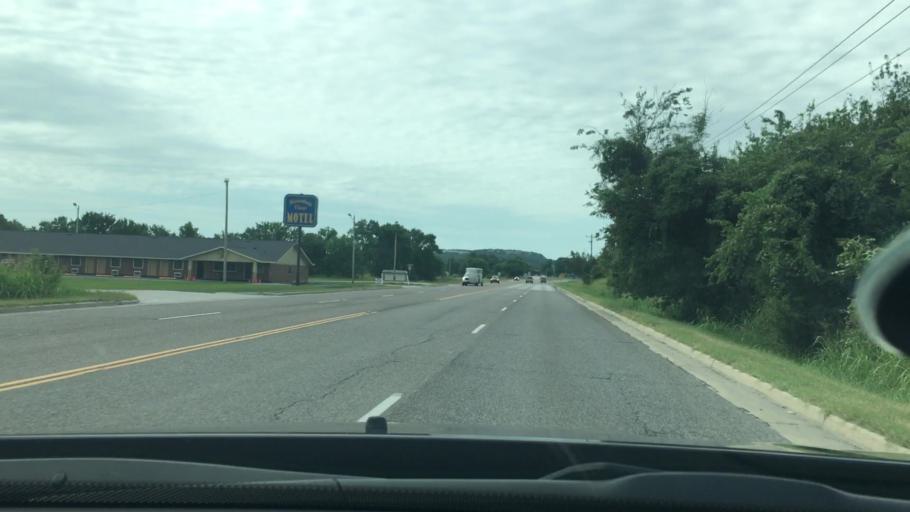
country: US
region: Oklahoma
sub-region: Murray County
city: Davis
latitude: 34.4683
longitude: -97.1312
